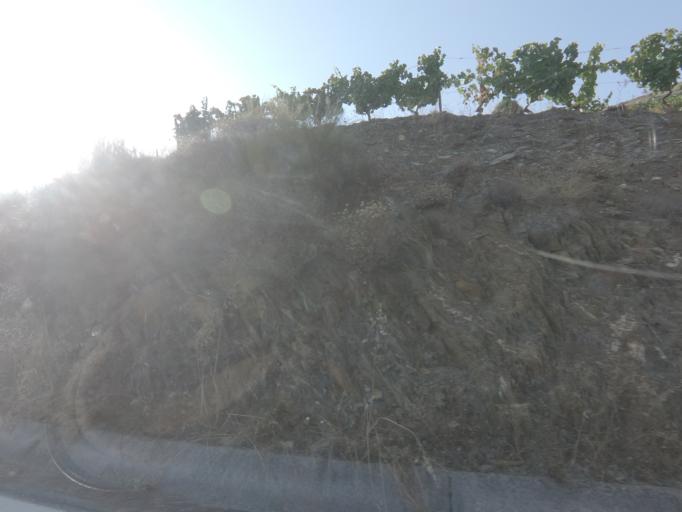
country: PT
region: Viseu
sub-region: Tabuaco
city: Tabuaco
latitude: 41.1396
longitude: -7.5387
